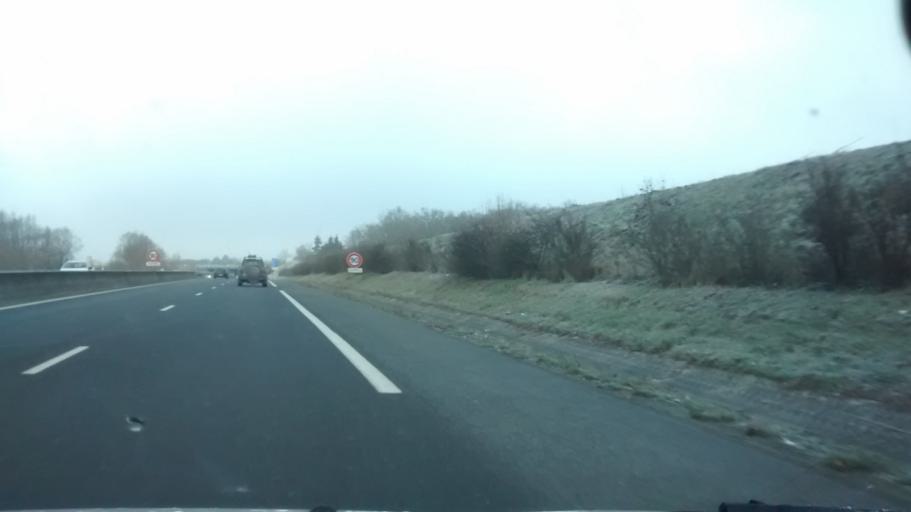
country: FR
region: Centre
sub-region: Departement d'Indre-et-Loire
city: Chambray-les-Tours
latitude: 47.3241
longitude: 0.6960
